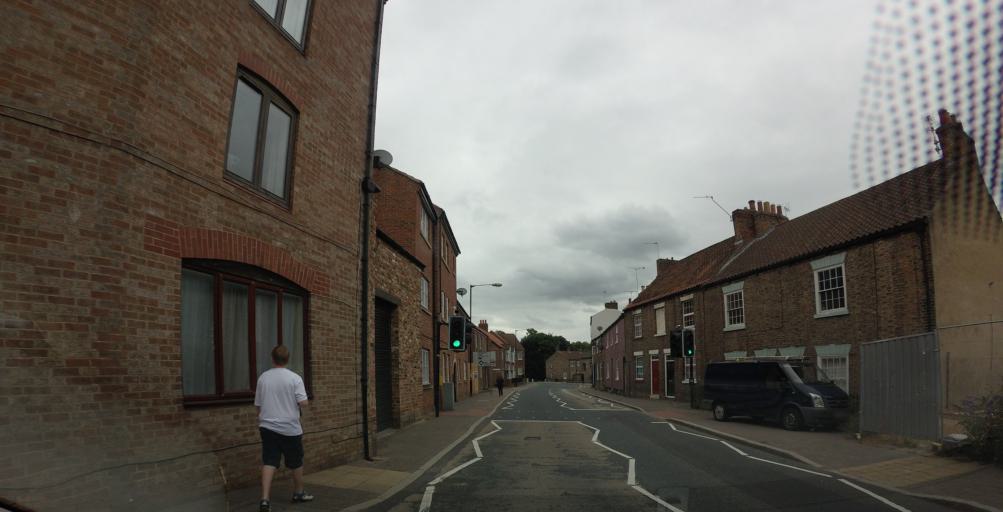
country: GB
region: England
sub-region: North Yorkshire
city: Ripon
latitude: 54.1349
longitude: -1.5227
